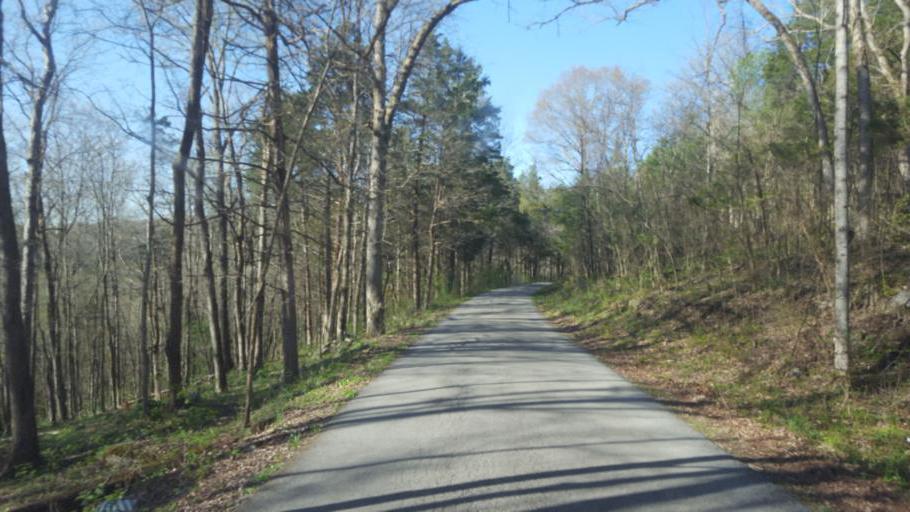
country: US
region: Kentucky
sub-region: Barren County
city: Cave City
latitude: 37.1998
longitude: -86.0343
